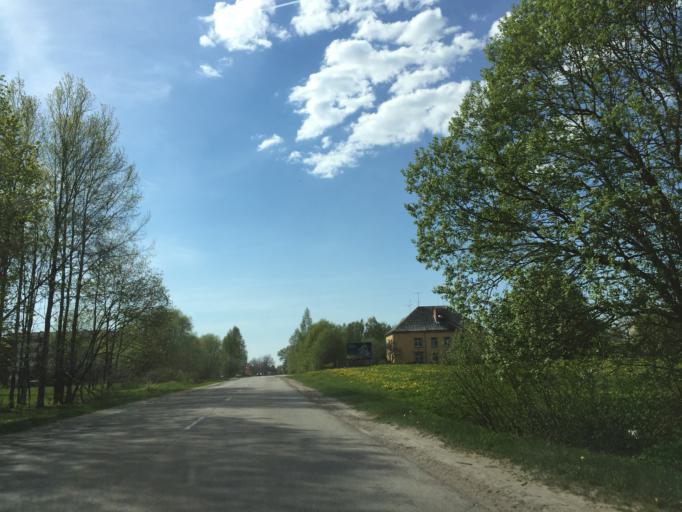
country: LV
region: Limbazu Rajons
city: Limbazi
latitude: 57.5120
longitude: 24.7344
